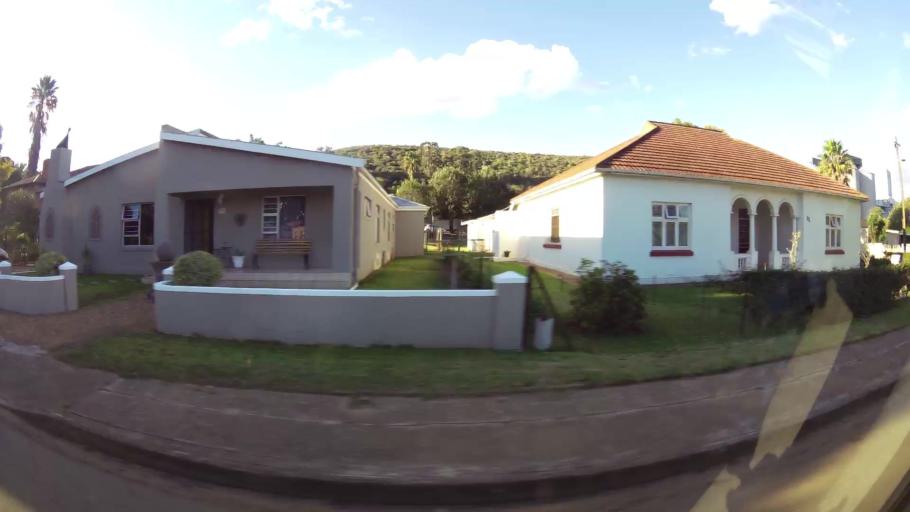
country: ZA
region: Western Cape
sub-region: Eden District Municipality
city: Riversdale
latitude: -34.0857
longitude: 20.9503
